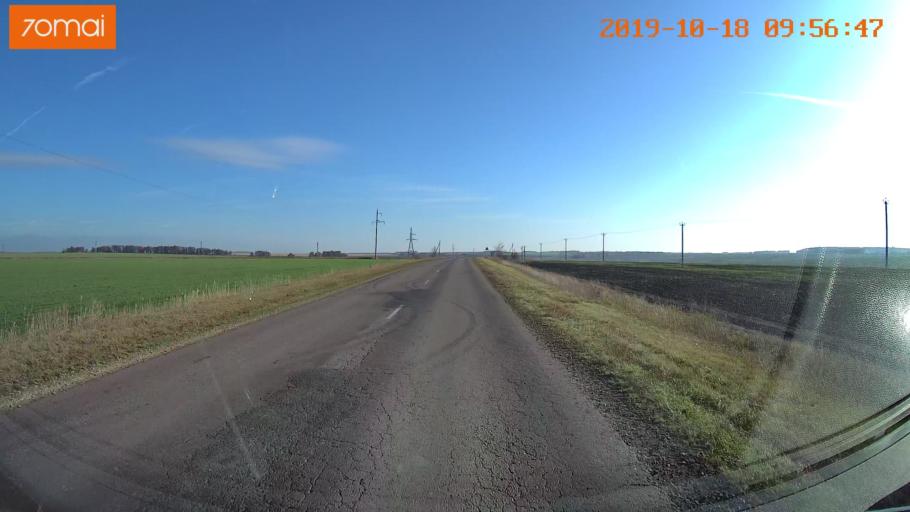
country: RU
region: Tula
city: Kurkino
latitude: 53.3754
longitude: 38.3990
